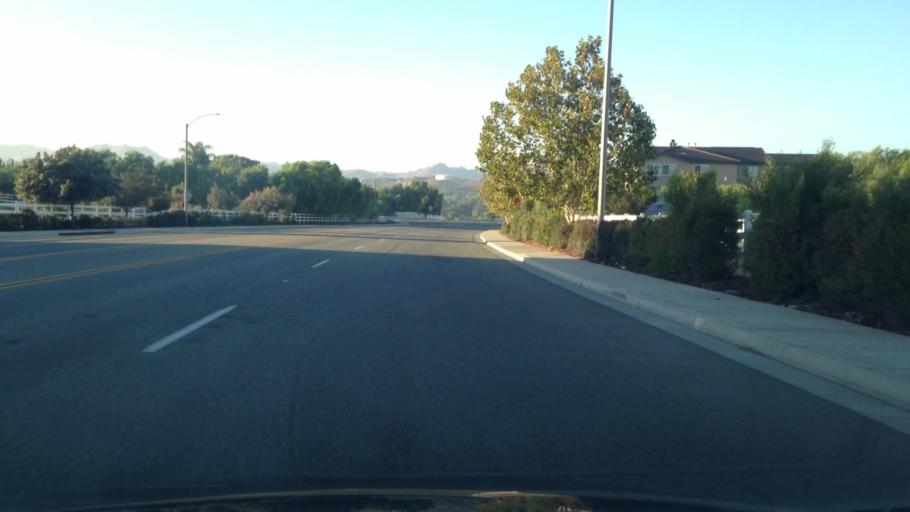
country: US
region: California
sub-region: Riverside County
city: Woodcrest
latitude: 33.8602
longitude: -117.3664
